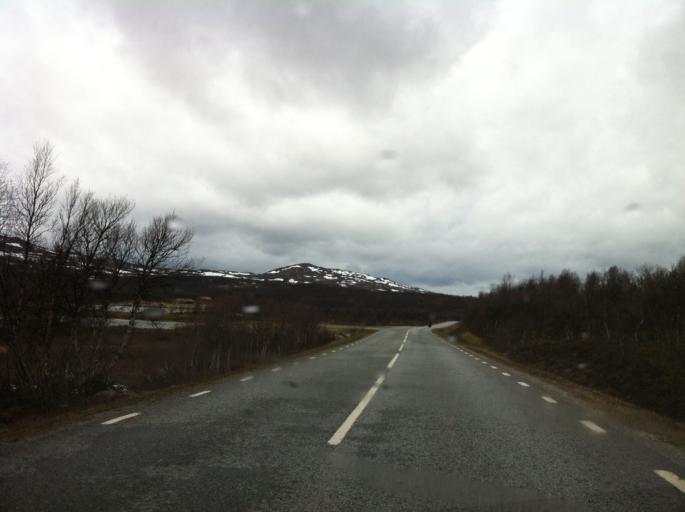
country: NO
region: Sor-Trondelag
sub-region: Tydal
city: Aas
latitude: 62.6136
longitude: 12.1483
